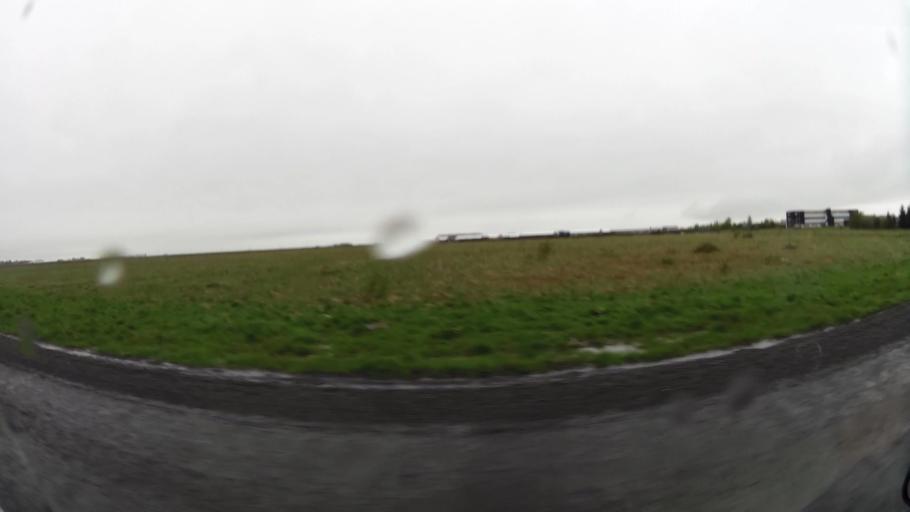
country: IS
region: South
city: Selfoss
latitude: 63.9305
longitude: -20.9761
